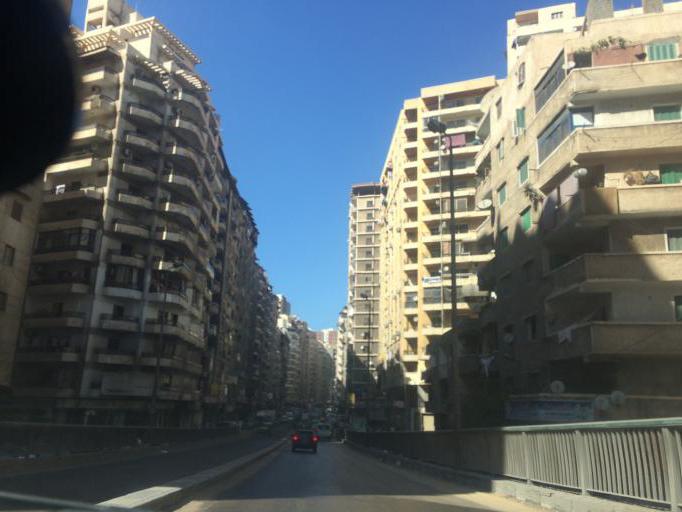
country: EG
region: Alexandria
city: Alexandria
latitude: 31.2687
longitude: 30.0009
